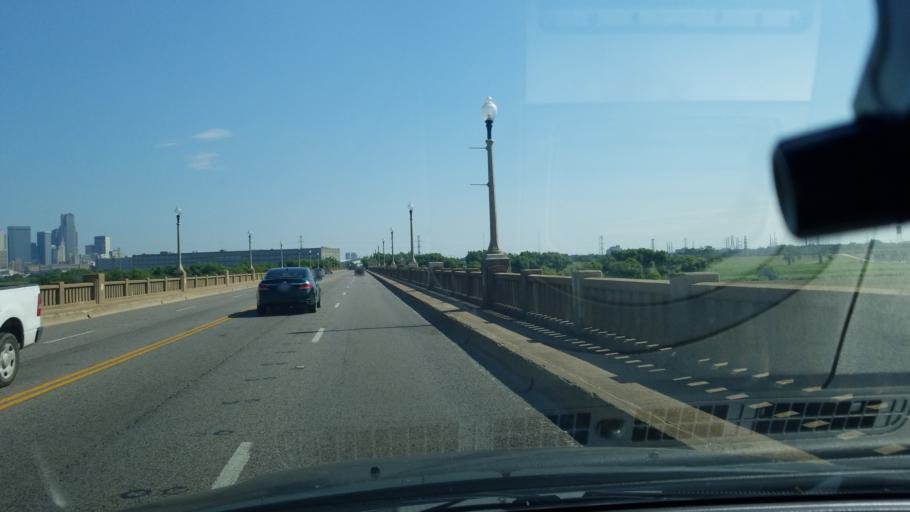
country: US
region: Texas
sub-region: Dallas County
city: Dallas
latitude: 32.7529
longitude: -96.7972
